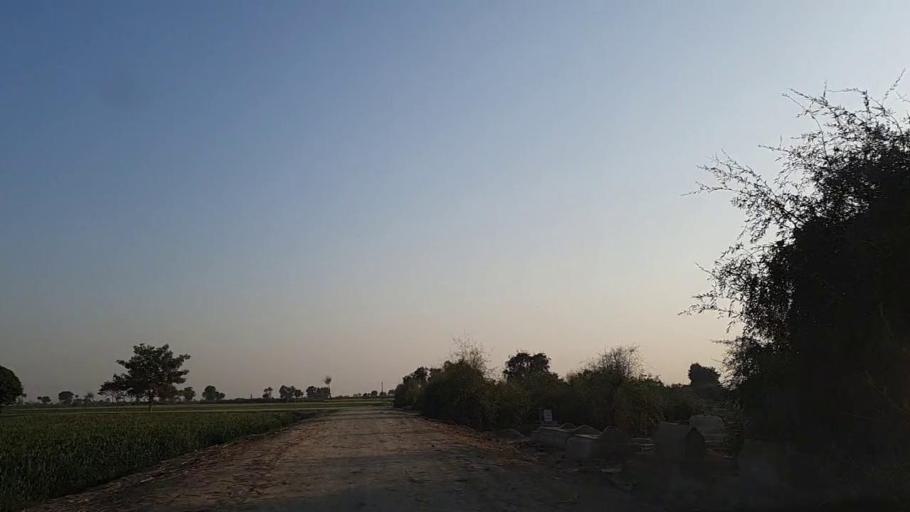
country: PK
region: Sindh
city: Daur
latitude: 26.5070
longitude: 68.2810
